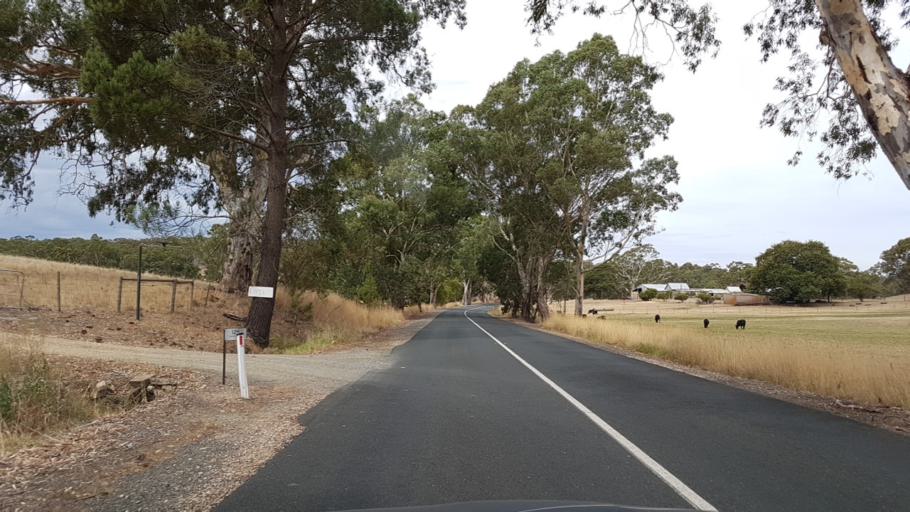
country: AU
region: South Australia
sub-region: Adelaide Hills
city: Birdwood
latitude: -34.7874
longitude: 138.9417
